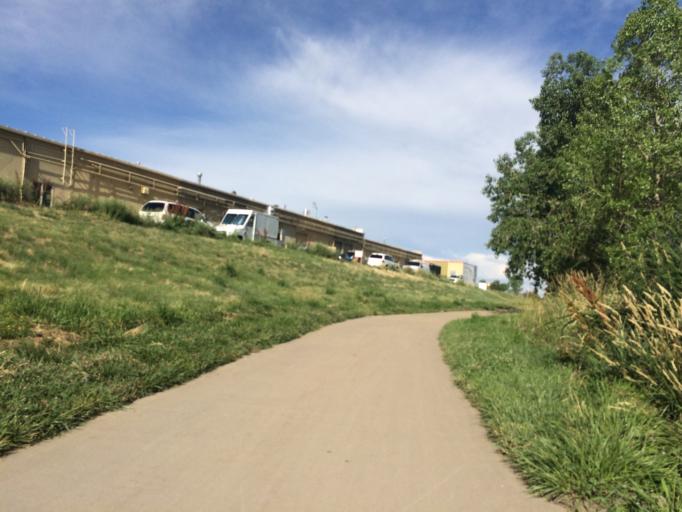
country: US
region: Colorado
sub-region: Boulder County
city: Boulder
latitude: 40.0254
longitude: -105.2500
